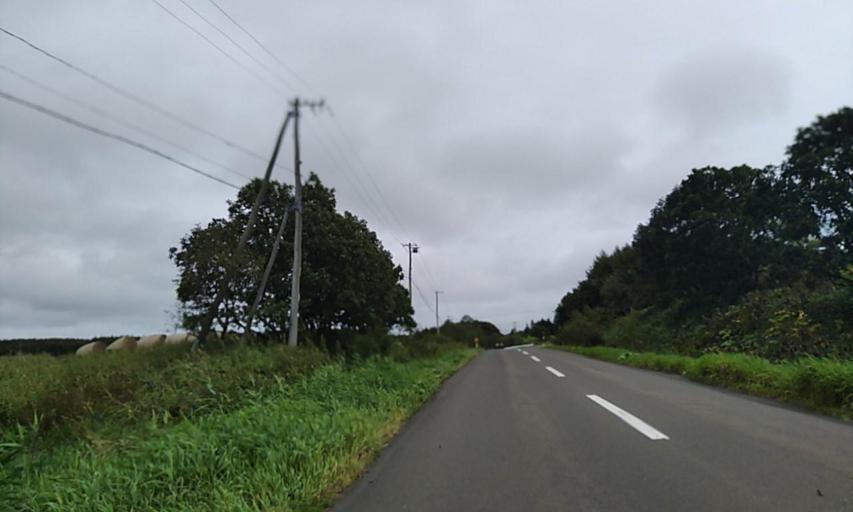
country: JP
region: Hokkaido
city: Nemuro
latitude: 43.2725
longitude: 145.2779
